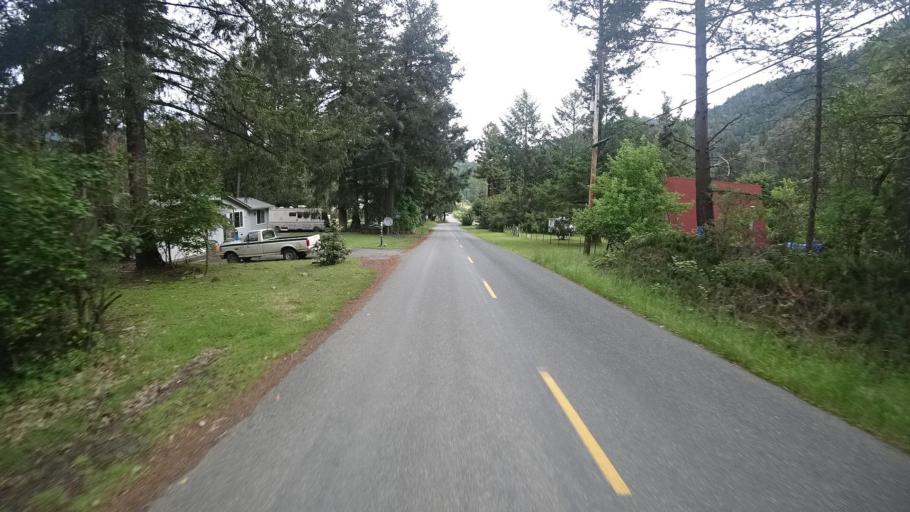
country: US
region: California
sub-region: Humboldt County
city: Willow Creek
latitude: 40.9711
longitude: -123.6305
